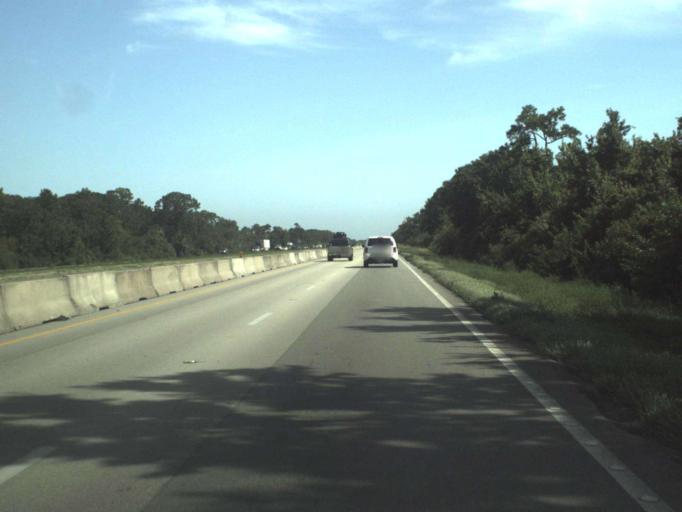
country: US
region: Florida
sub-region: Indian River County
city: Fellsmere
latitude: 27.7076
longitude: -80.5417
